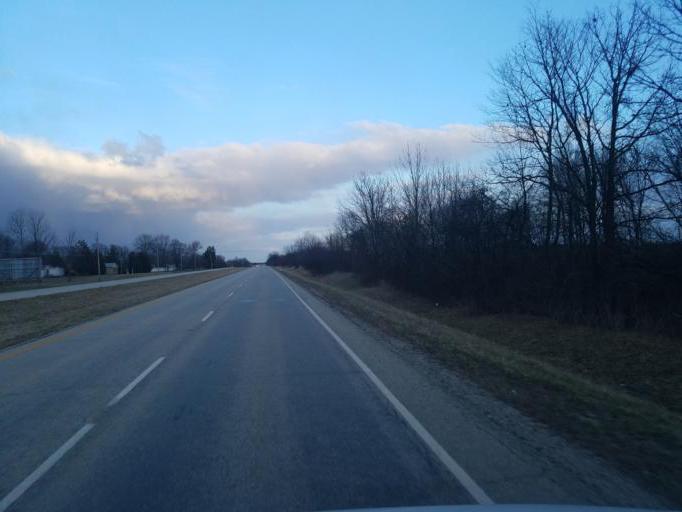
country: US
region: Indiana
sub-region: Henry County
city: Knightstown
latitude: 39.8021
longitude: -85.4843
